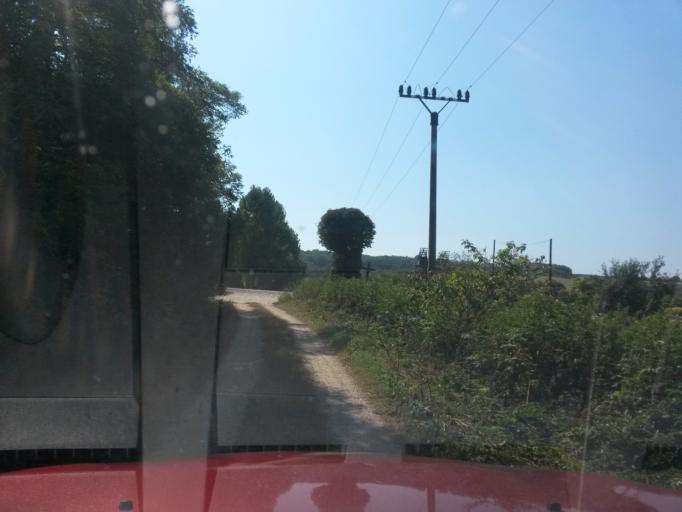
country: HU
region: Borsod-Abauj-Zemplen
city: Gonc
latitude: 48.5337
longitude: 21.1574
